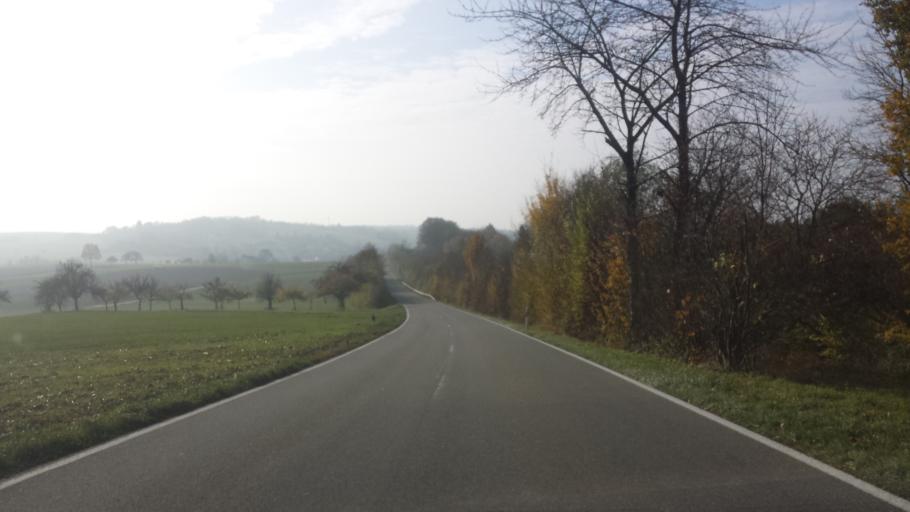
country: DE
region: Baden-Wuerttemberg
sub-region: Karlsruhe Region
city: Binau
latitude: 49.3494
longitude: 9.0372
